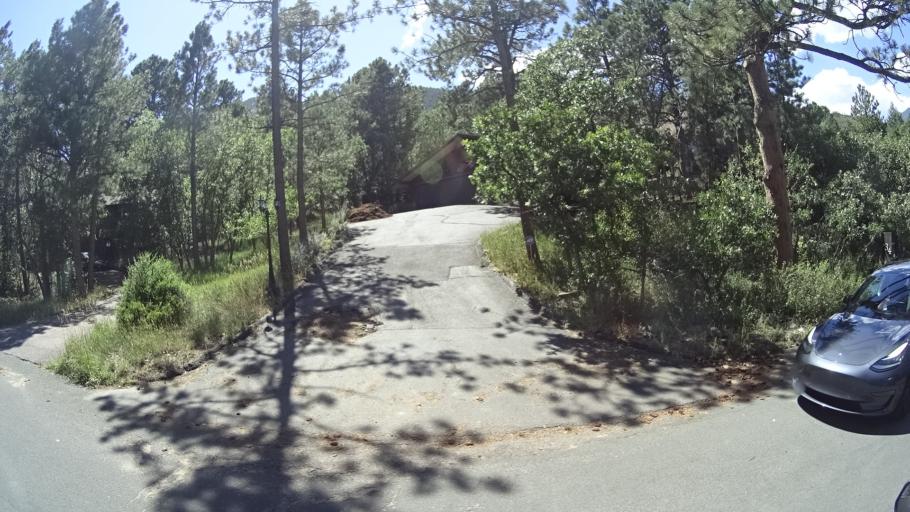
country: US
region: Colorado
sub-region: El Paso County
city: Colorado Springs
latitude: 38.7830
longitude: -104.8613
